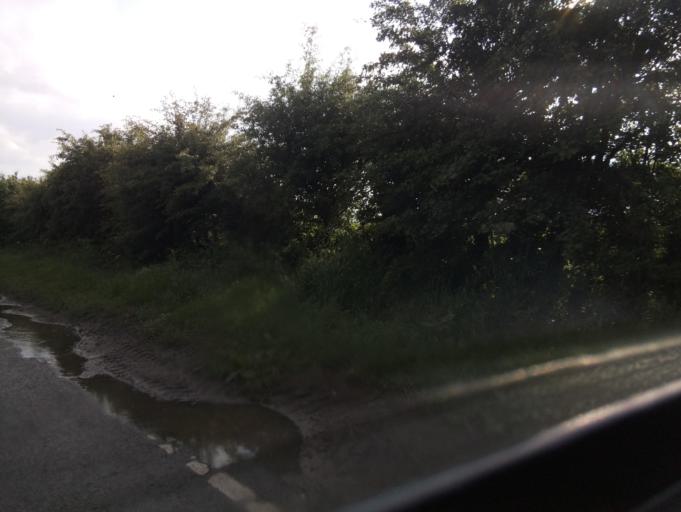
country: GB
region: England
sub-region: Lincolnshire
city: Great Gonerby
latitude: 52.9792
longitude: -0.6773
